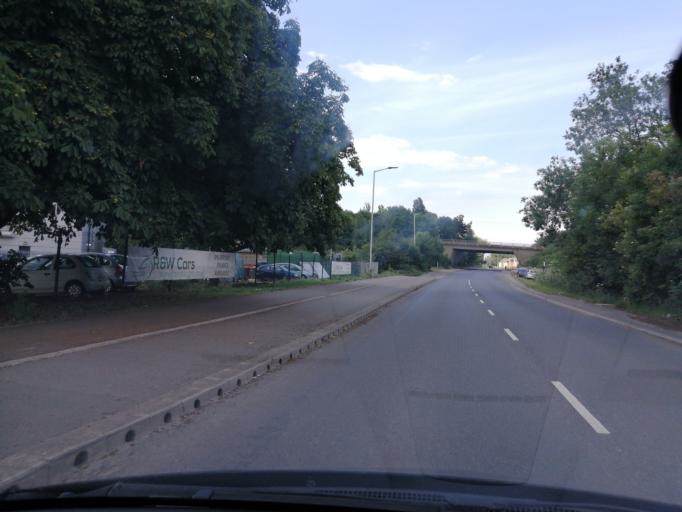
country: GB
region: England
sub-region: Peterborough
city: Peterborough
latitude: 52.5465
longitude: -0.2513
